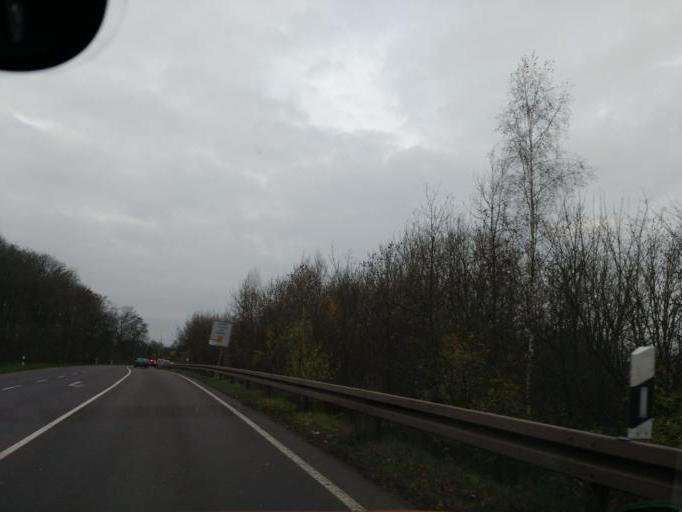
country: DE
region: Lower Saxony
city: Laatzen
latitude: 52.3612
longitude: 9.8680
